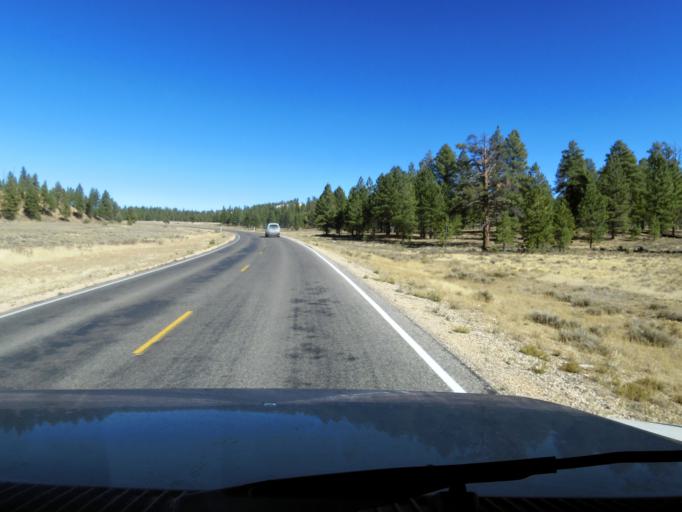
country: US
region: Utah
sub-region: Garfield County
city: Panguitch
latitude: 37.6073
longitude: -112.1855
